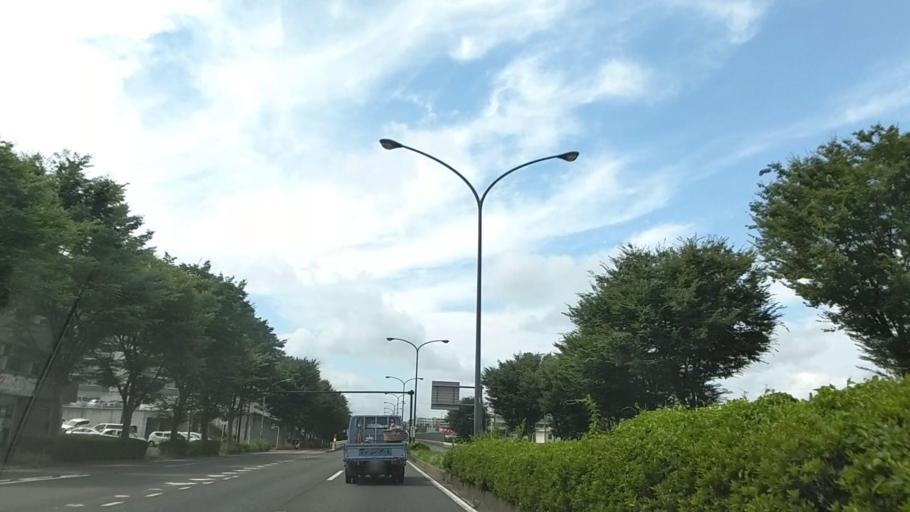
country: JP
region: Kanagawa
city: Yokohama
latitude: 35.4234
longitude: 139.5609
